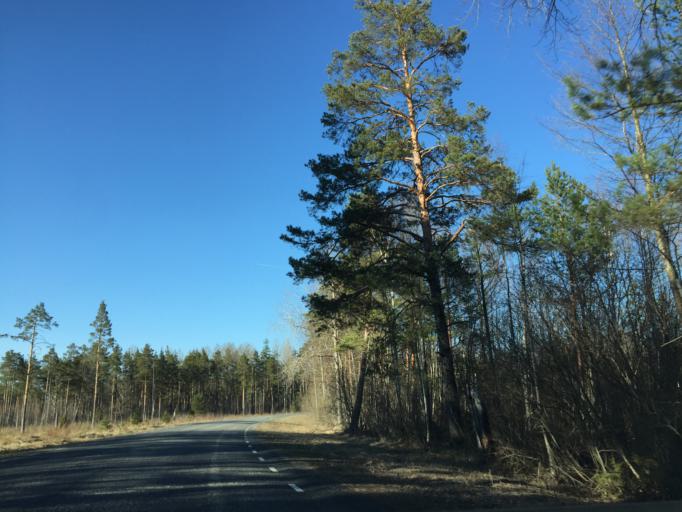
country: RU
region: Pskov
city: Gdov
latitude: 59.0126
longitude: 27.6817
